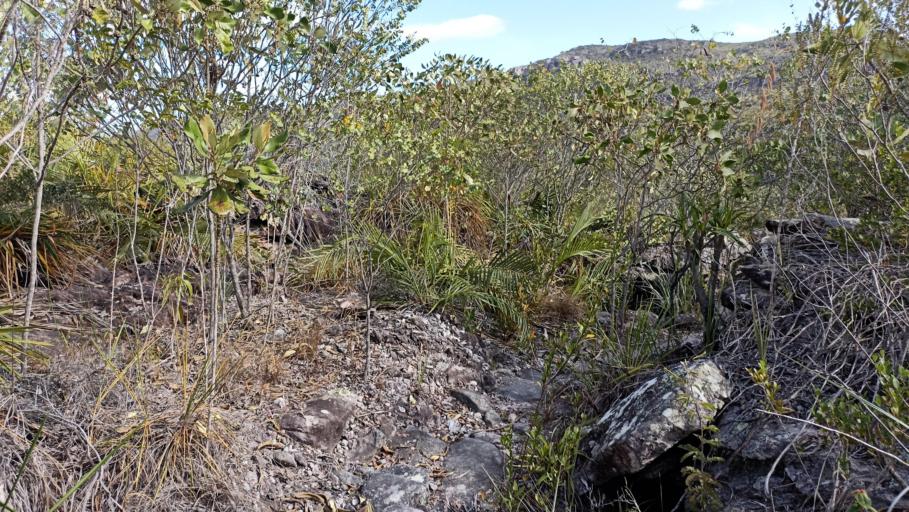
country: BR
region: Bahia
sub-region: Andarai
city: Vera Cruz
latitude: -12.9990
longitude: -41.3764
